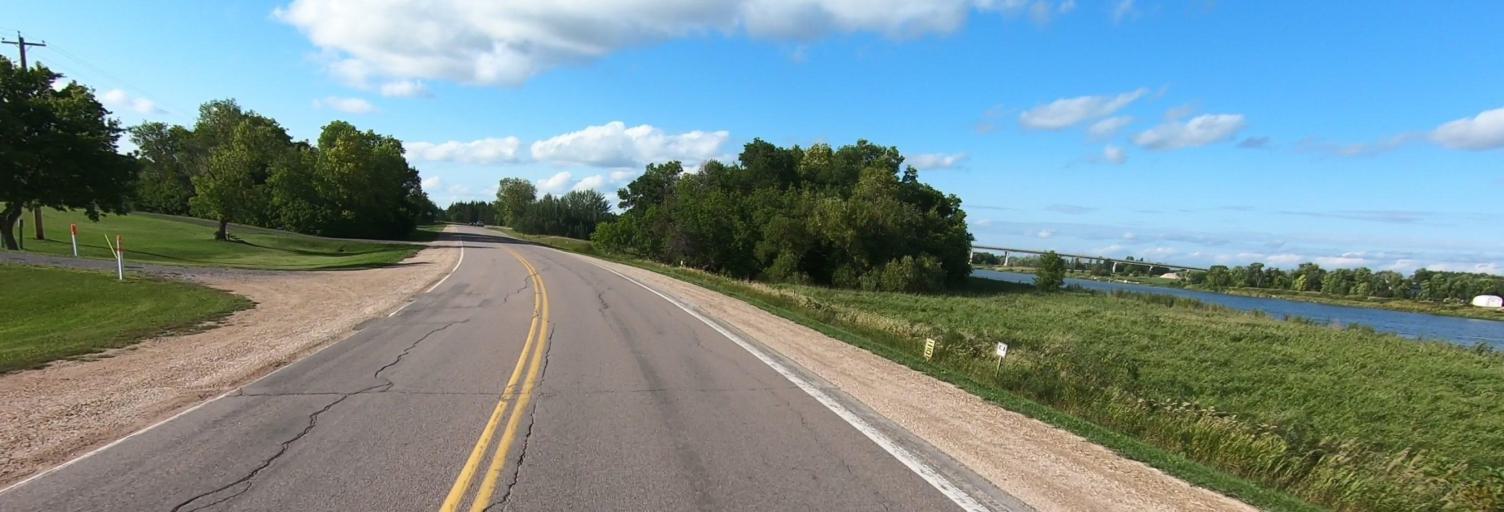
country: CA
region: Manitoba
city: Selkirk
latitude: 50.1840
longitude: -96.8443
